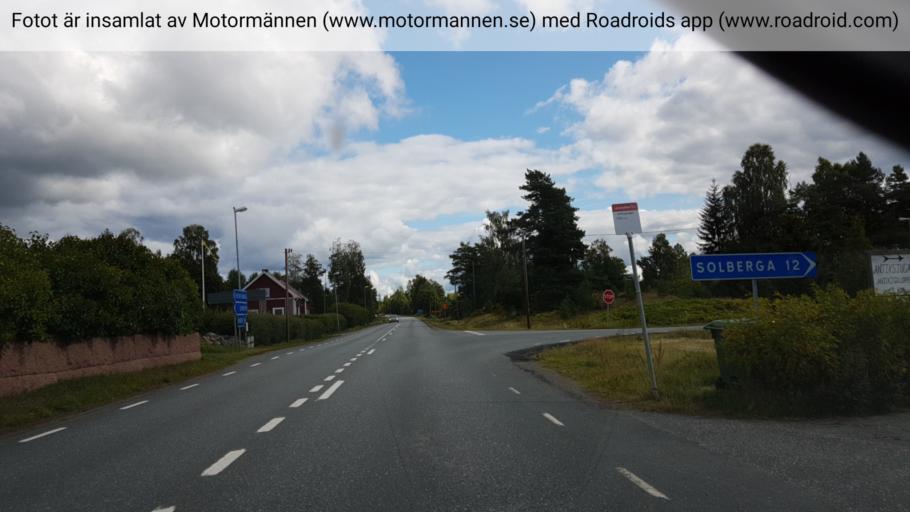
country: SE
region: Joenkoeping
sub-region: Aneby Kommun
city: Hestra
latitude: 57.7767
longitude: 14.5975
